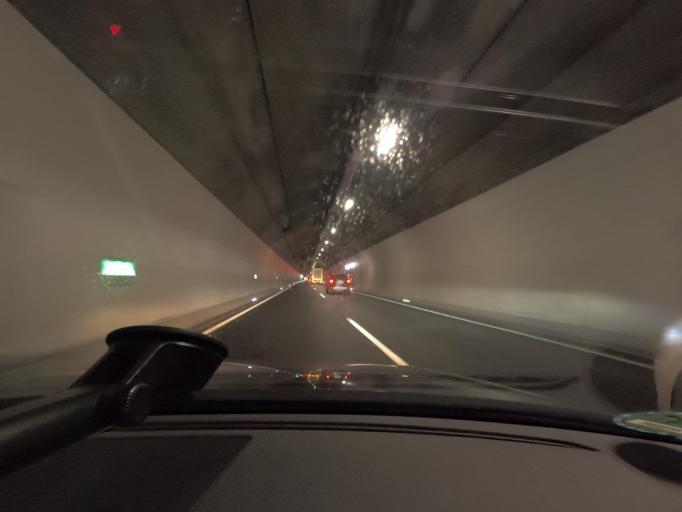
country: DE
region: Thuringia
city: Geschwenda
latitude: 50.7172
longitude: 10.8104
